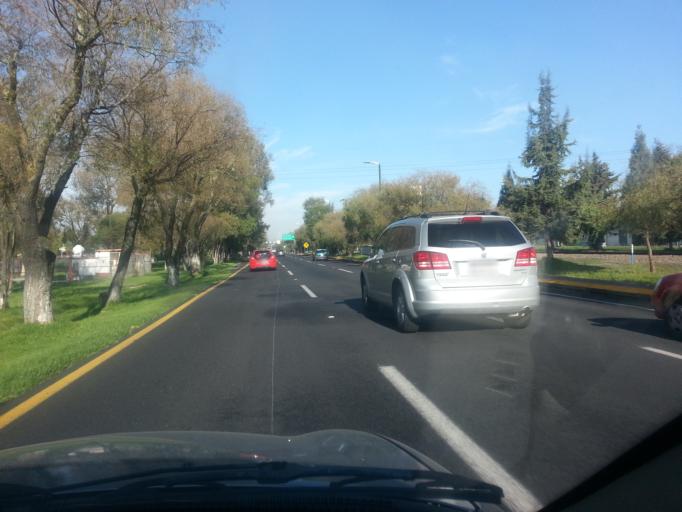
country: MX
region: Mexico
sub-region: San Mateo Atenco
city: Santa Maria la Asuncion
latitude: 19.2866
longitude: -99.5651
